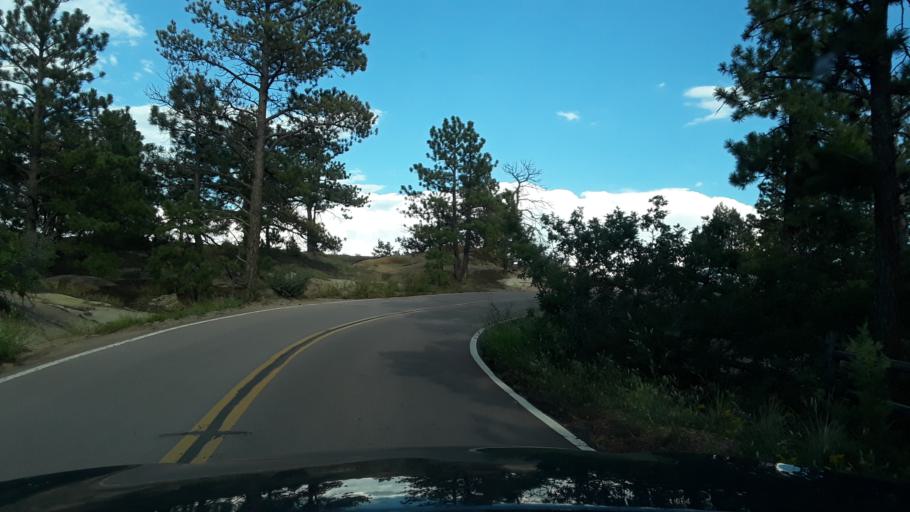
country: US
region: Colorado
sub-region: El Paso County
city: Colorado Springs
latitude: 38.8791
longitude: -104.7685
